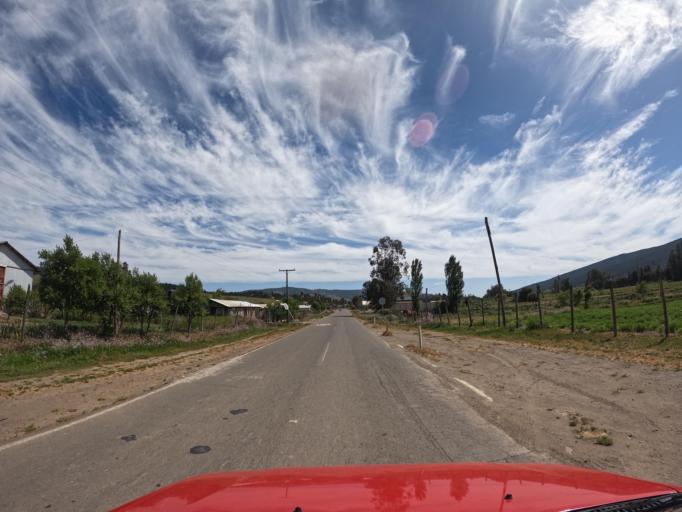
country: CL
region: Maule
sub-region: Provincia de Talca
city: Constitucion
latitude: -35.0246
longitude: -72.0441
